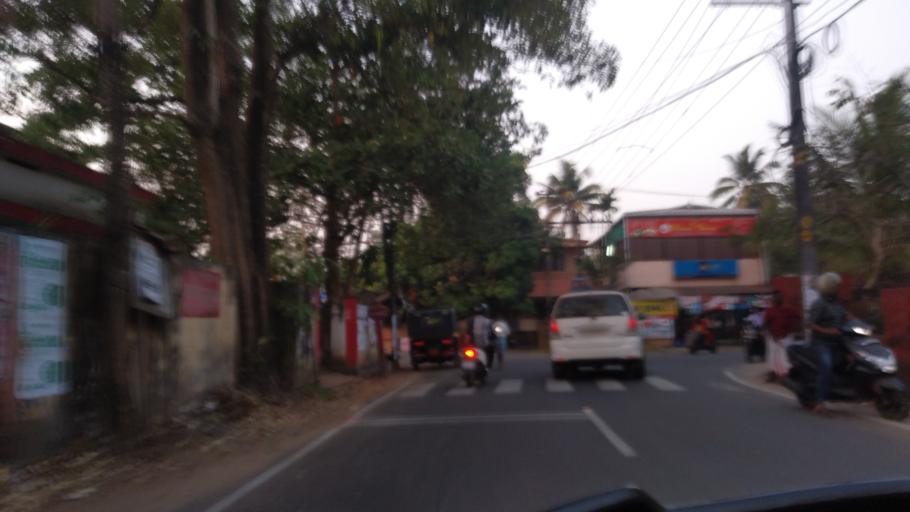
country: IN
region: Kerala
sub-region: Ernakulam
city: Elur
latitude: 10.1364
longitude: 76.2306
